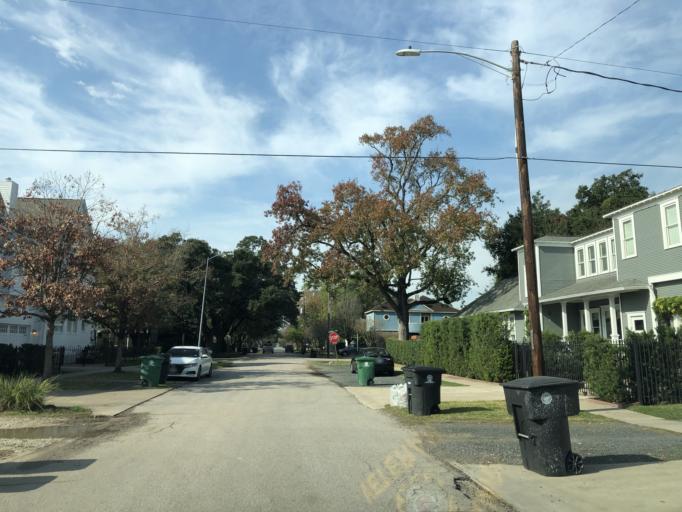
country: US
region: Texas
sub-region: Harris County
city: Houston
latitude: 29.7944
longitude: -95.3957
